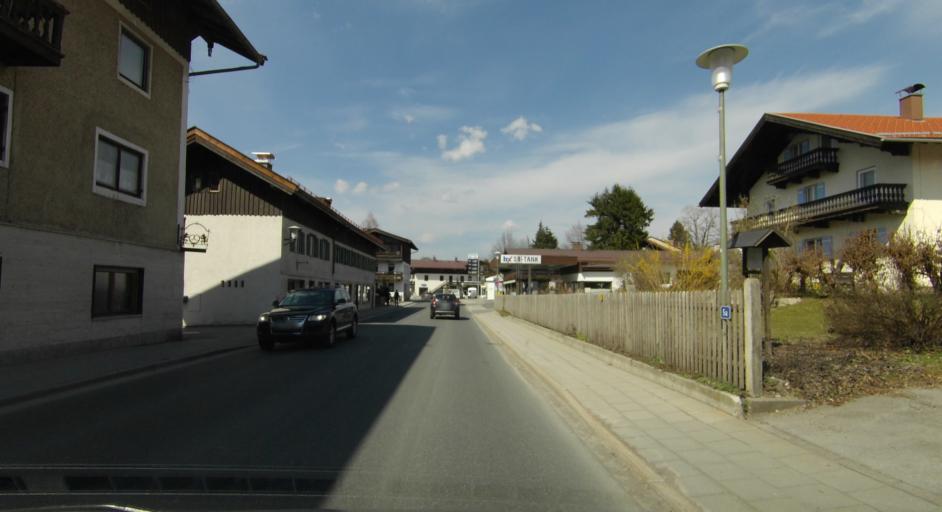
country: DE
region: Bavaria
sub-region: Upper Bavaria
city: Schliersee
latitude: 47.7365
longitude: 11.8604
